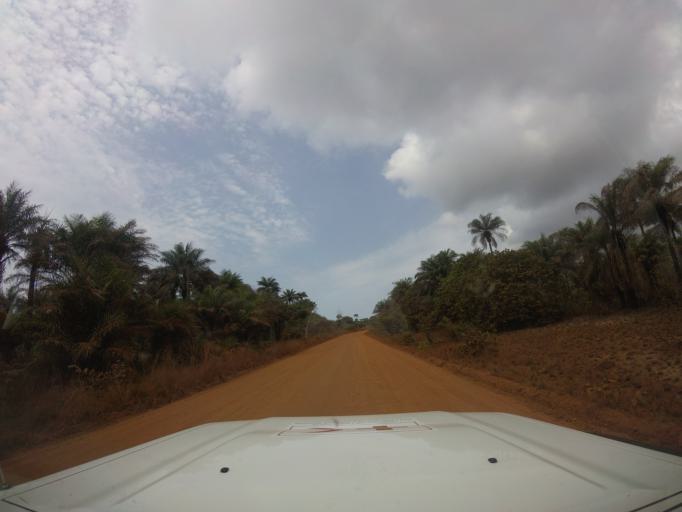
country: LR
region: Grand Cape Mount
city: Robertsport
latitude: 6.7039
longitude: -11.3070
